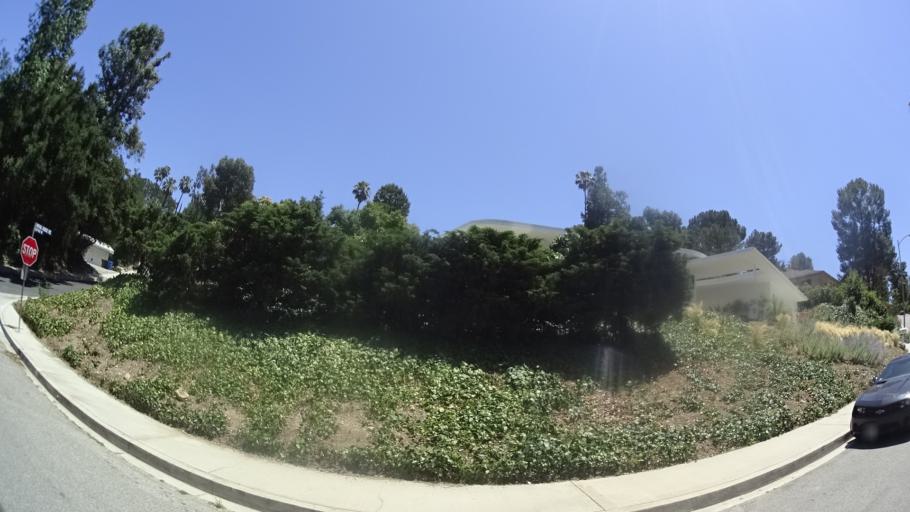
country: US
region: California
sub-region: Los Angeles County
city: Sherman Oaks
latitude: 34.1398
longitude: -118.4761
